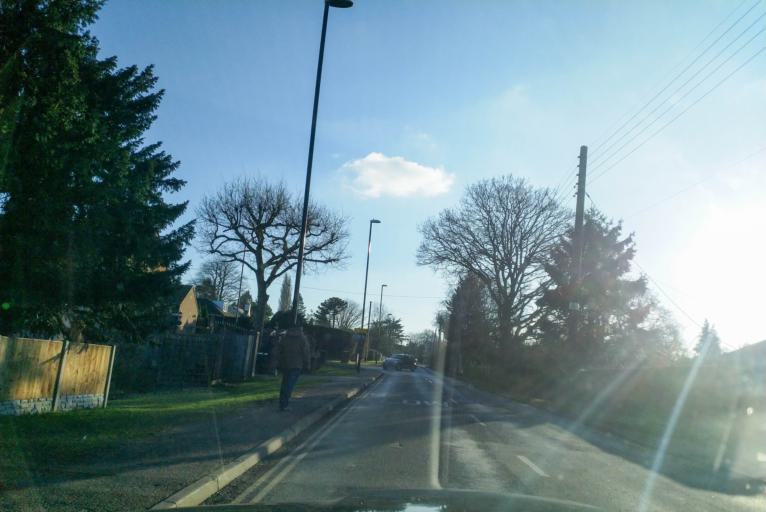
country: GB
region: England
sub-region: Warwickshire
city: Kenilworth
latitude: 52.3935
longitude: -1.5968
